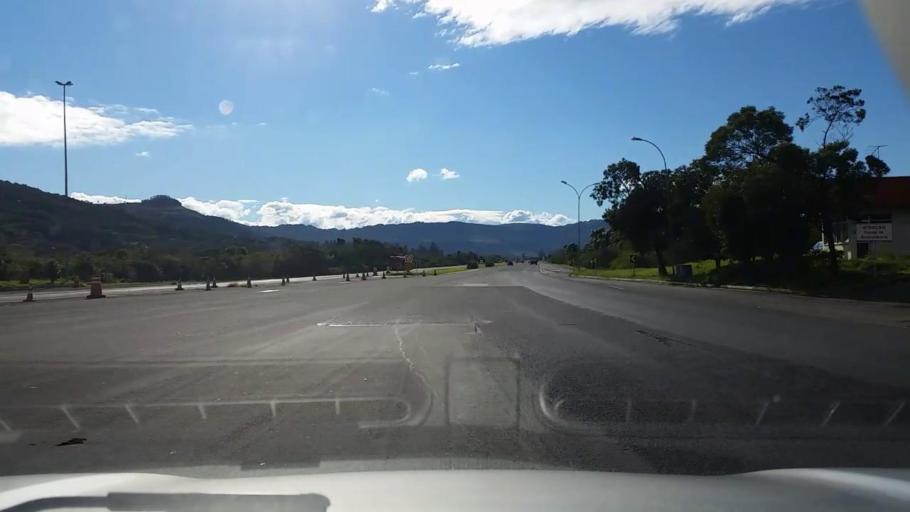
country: BR
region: Rio Grande do Sul
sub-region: Osorio
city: Osorio
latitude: -29.8847
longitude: -50.4450
